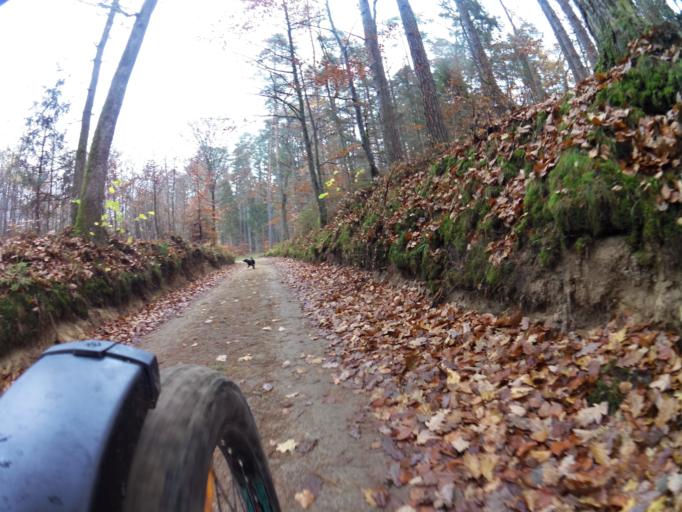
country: PL
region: Pomeranian Voivodeship
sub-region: Powiat wejherowski
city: Orle
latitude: 54.6959
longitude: 18.1566
